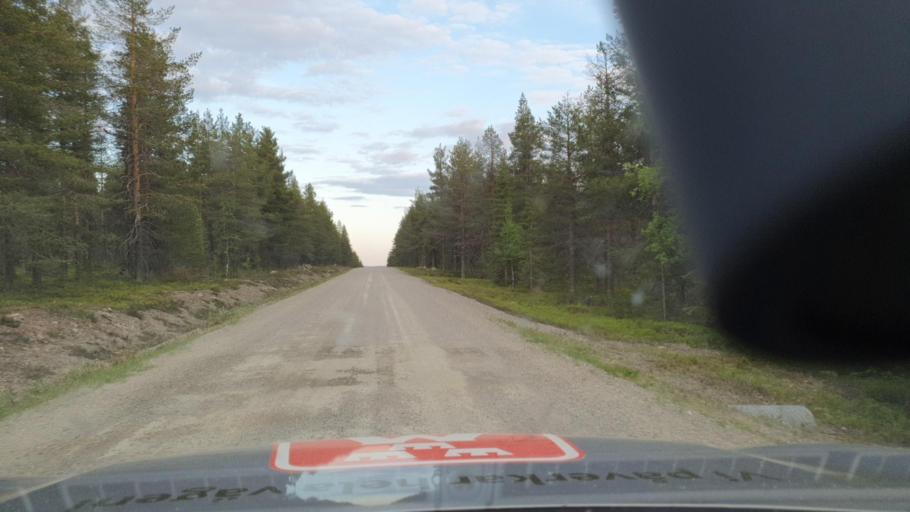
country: SE
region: Norrbotten
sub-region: Gallivare Kommun
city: Gaellivare
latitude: 66.6219
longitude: 21.3441
